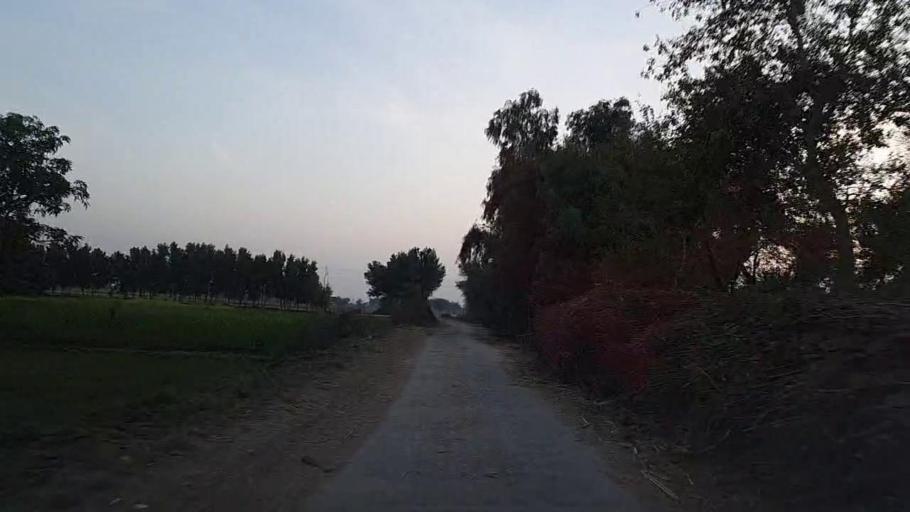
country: PK
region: Sindh
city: Tando Mittha Khan
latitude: 25.9433
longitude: 69.1546
